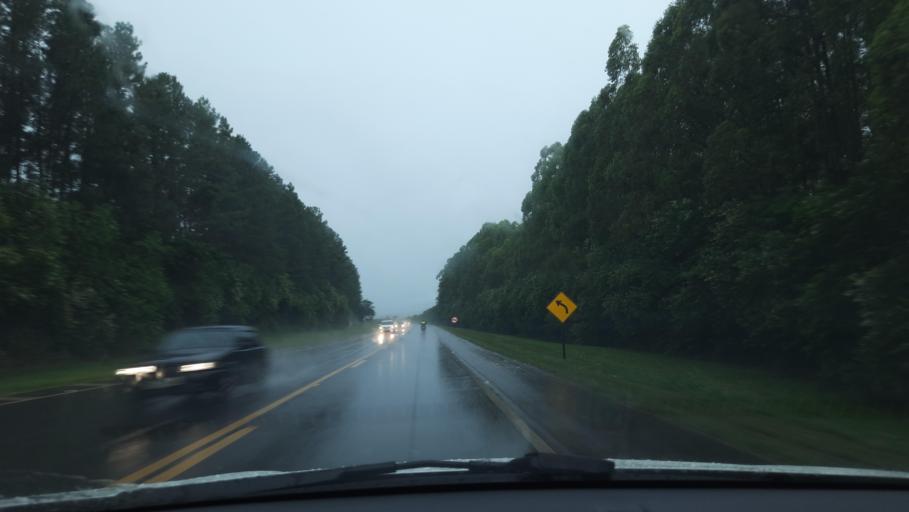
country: BR
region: Sao Paulo
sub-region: Casa Branca
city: Casa Branca
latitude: -21.7580
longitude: -47.0086
